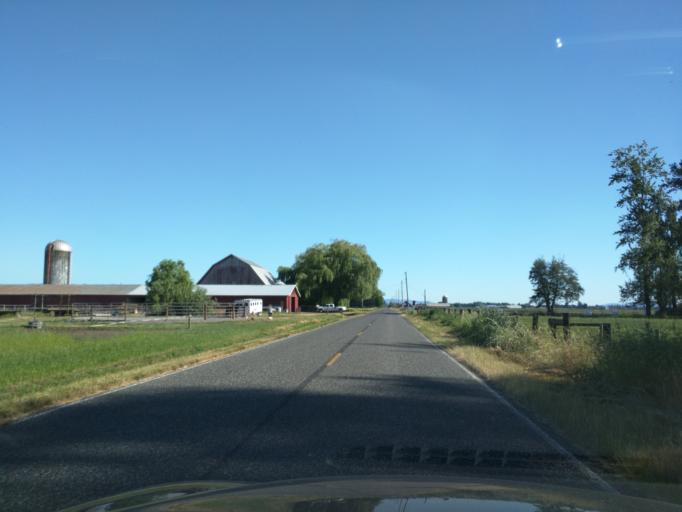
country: US
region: Washington
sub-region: Whatcom County
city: Lynden
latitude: 48.9810
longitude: -122.4405
